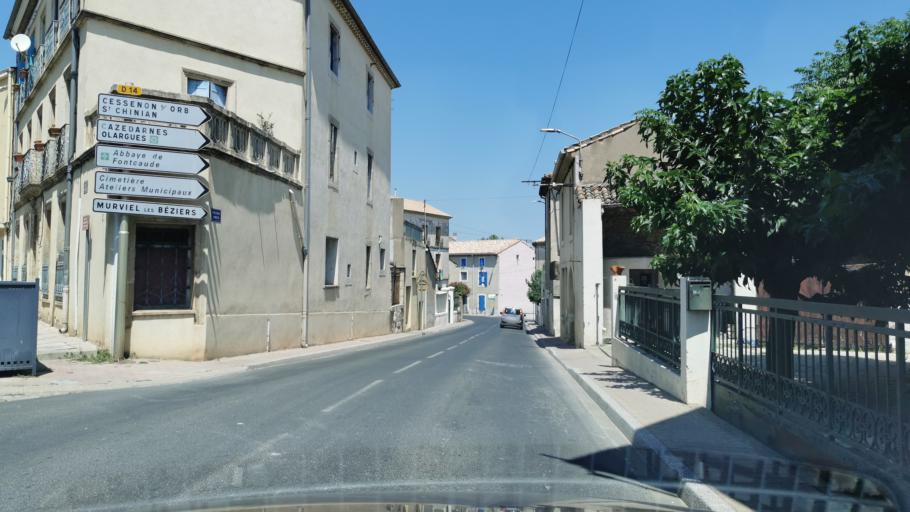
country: FR
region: Languedoc-Roussillon
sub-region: Departement de l'Herault
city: Cazouls-les-Beziers
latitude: 43.3926
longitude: 3.1022
